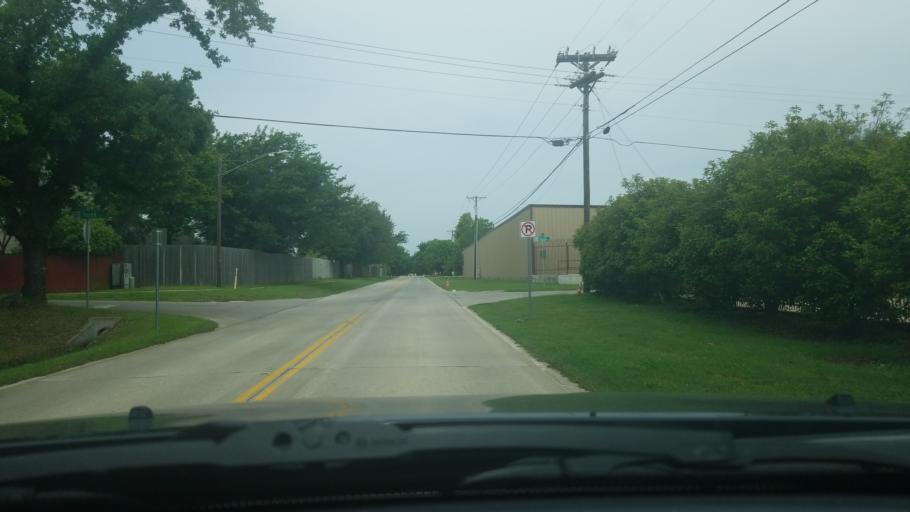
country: US
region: Texas
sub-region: Denton County
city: Lake Dallas
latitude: 33.1092
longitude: -97.0125
